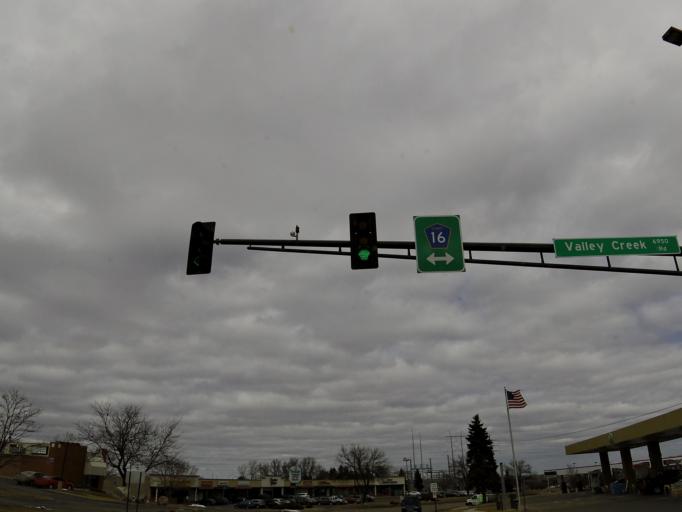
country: US
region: Minnesota
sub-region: Washington County
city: Woodbury
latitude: 44.9253
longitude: -92.9661
